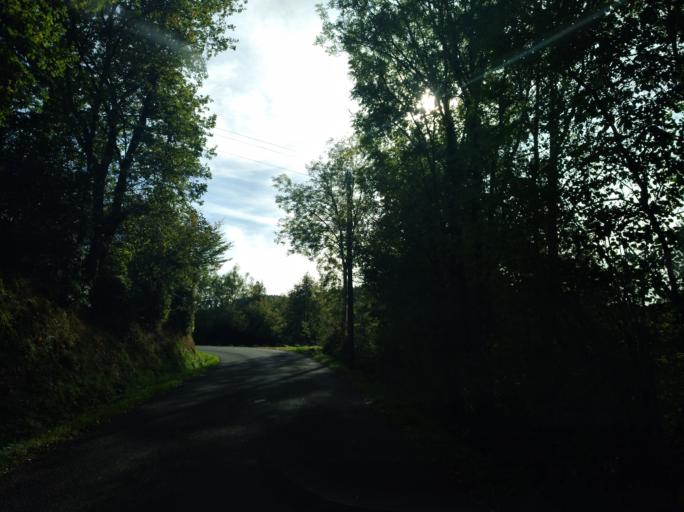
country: FR
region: Rhone-Alpes
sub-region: Departement de la Loire
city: Belmont-de-la-Loire
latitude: 46.1937
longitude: 4.4127
